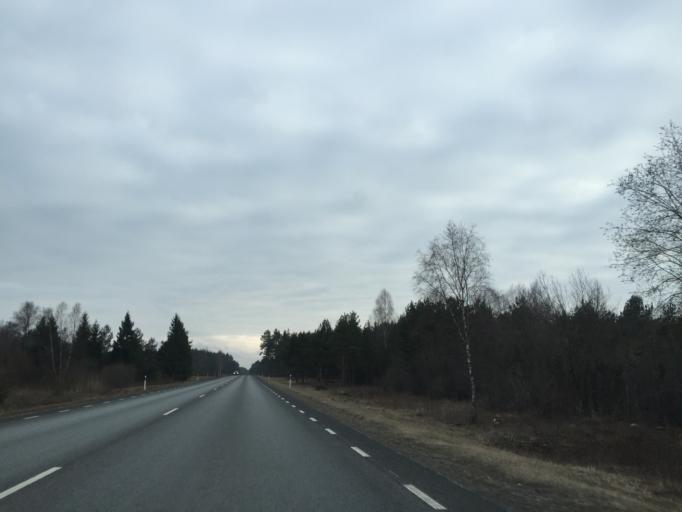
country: EE
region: Saare
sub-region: Orissaare vald
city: Orissaare
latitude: 58.5088
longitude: 22.8716
